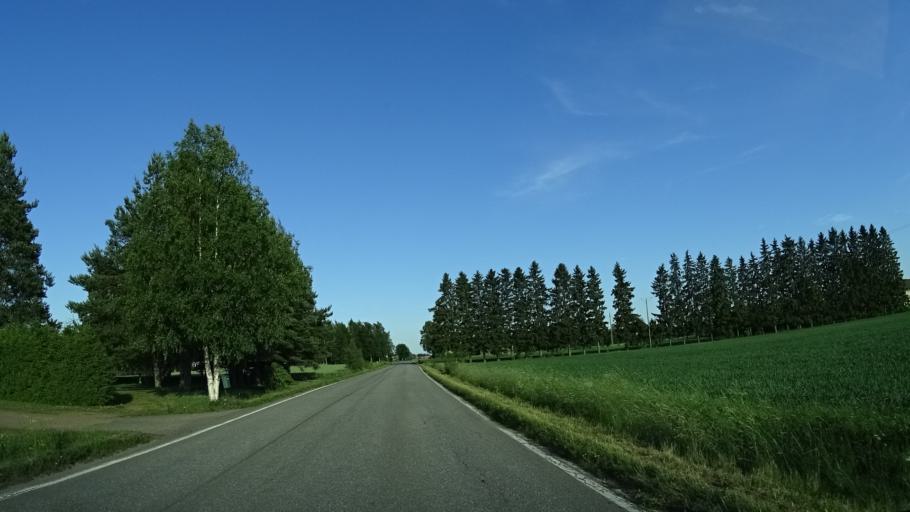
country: FI
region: Satakunta
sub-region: Pori
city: Kokemaeki
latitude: 61.2807
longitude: 22.2535
